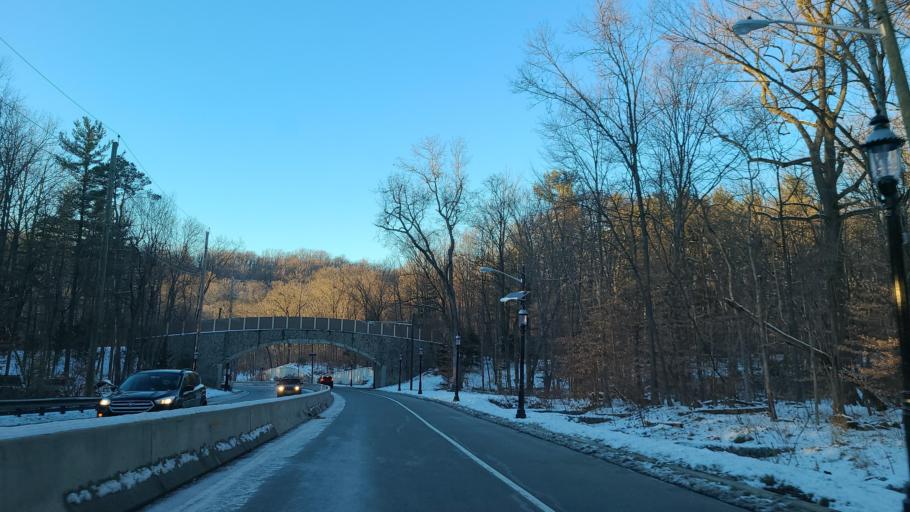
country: US
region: New Jersey
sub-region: Essex County
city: Maplewood
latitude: 40.7527
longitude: -74.2895
